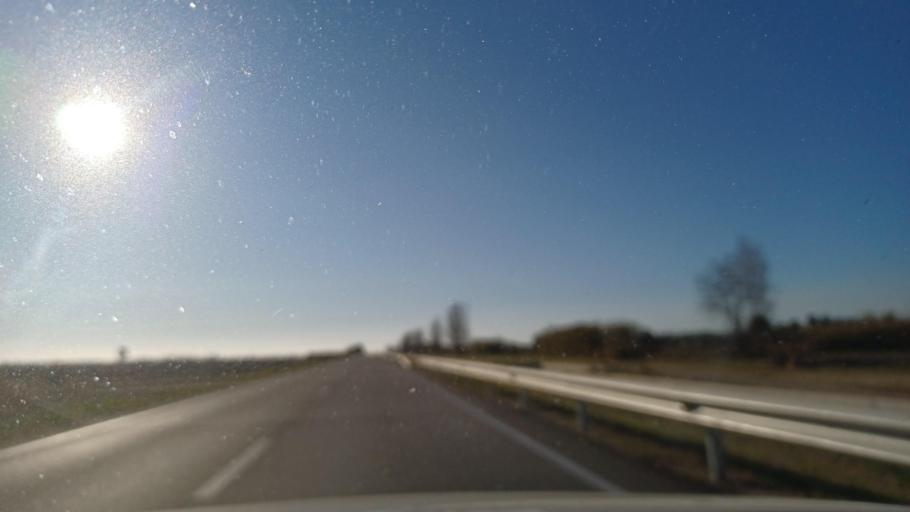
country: ES
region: Catalonia
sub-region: Provincia de Tarragona
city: Sant Carles de la Rapita
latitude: 40.6524
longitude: 0.5958
